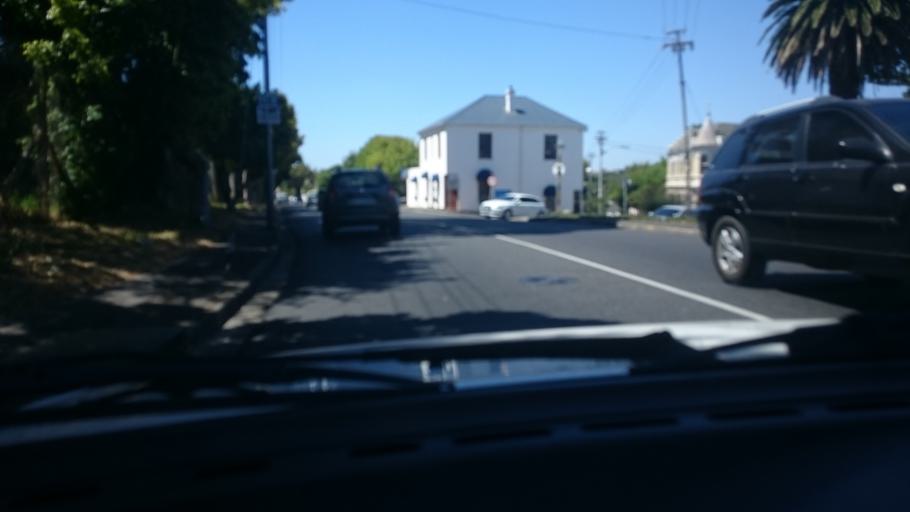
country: ZA
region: Western Cape
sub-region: City of Cape Town
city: Claremont
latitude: -34.0095
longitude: 18.4619
